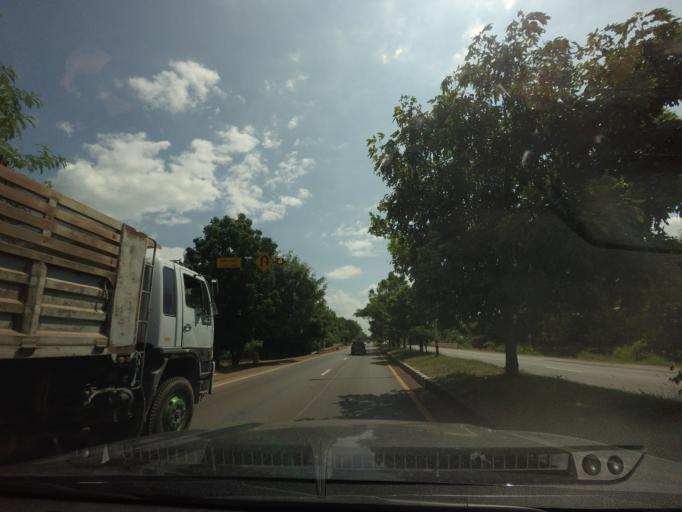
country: TH
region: Phetchabun
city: Nong Phai
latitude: 15.9291
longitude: 101.0263
